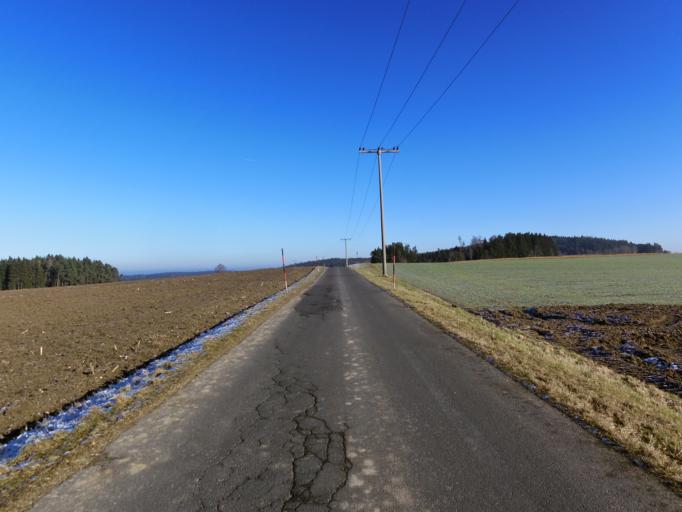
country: DE
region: Bavaria
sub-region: Upper Franconia
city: Roslau
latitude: 50.0811
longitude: 12.0206
